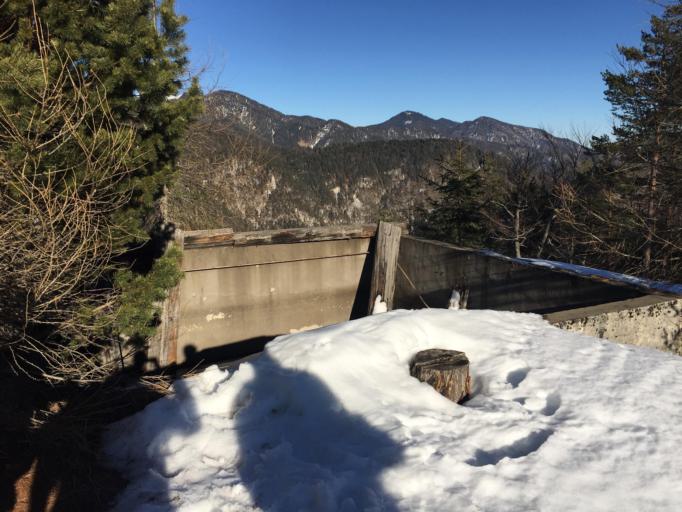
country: IT
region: Friuli Venezia Giulia
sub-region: Provincia di Udine
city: Malborghetto
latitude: 46.5028
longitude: 13.4712
